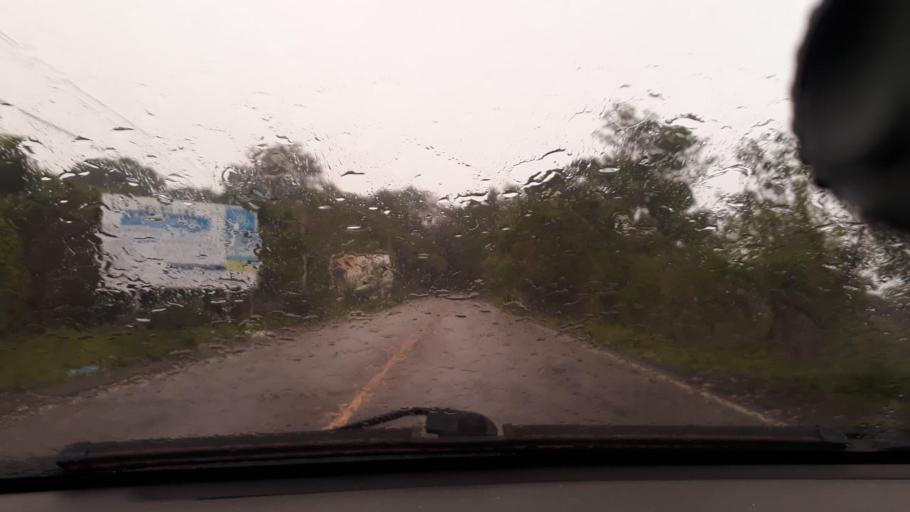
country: GT
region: Jutiapa
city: Comapa
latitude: 14.0263
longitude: -89.9084
